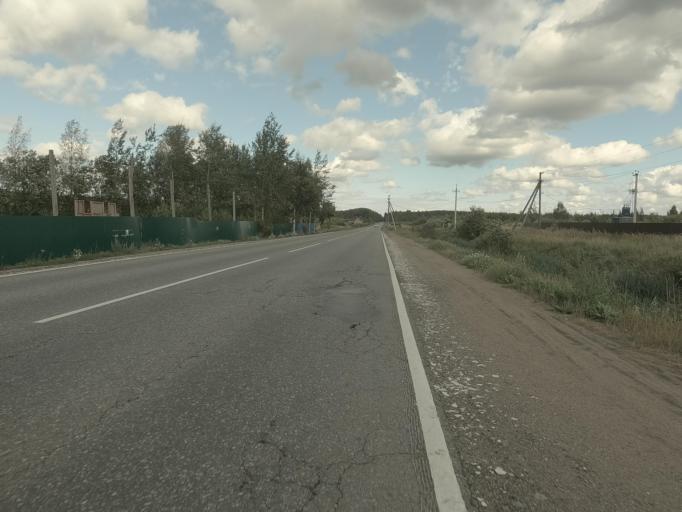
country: RU
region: Leningrad
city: Shcheglovo
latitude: 60.0291
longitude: 30.7801
